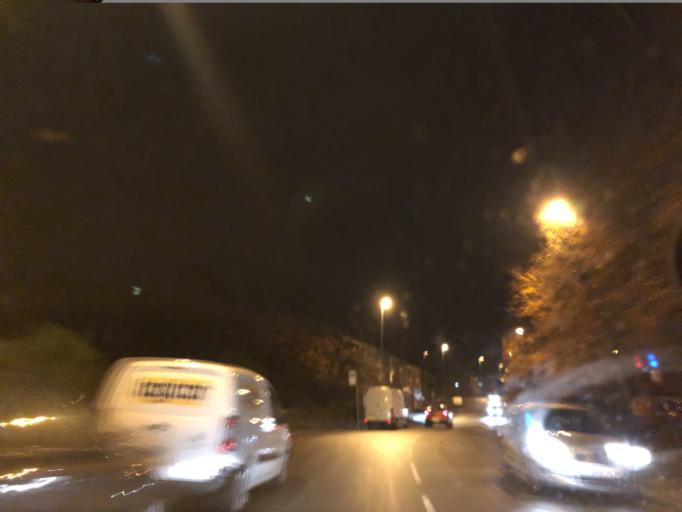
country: GB
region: England
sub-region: Borough of Oldham
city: Oldham
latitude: 53.5252
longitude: -2.1156
